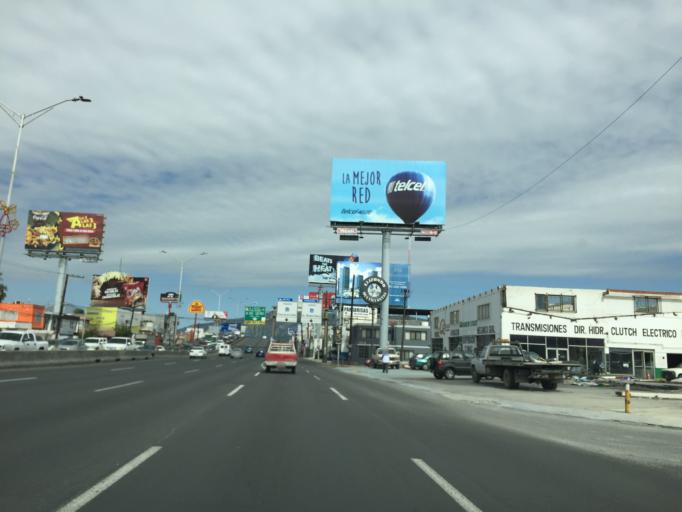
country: MX
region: Nuevo Leon
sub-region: Monterrey
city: Monterrey
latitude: 25.6942
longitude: -100.3512
